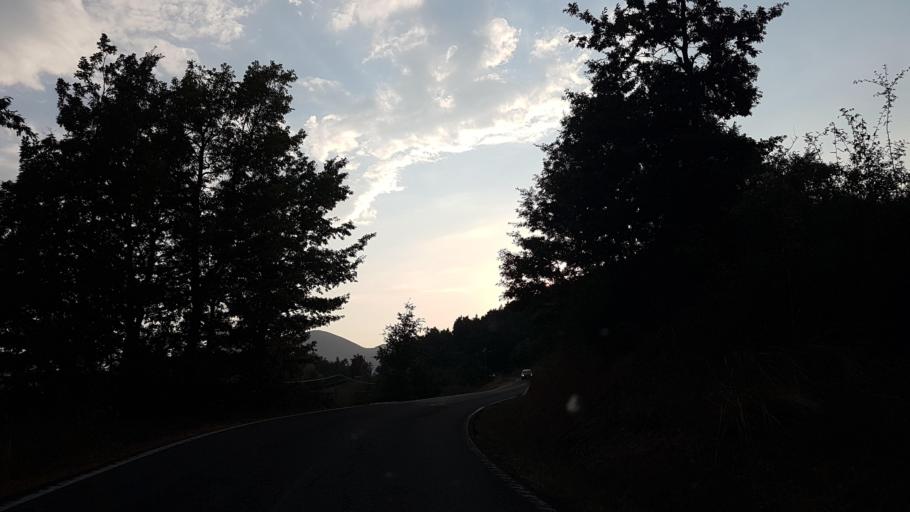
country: IT
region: Emilia-Romagna
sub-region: Provincia di Parma
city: Albareto
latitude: 44.4569
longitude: 9.6820
